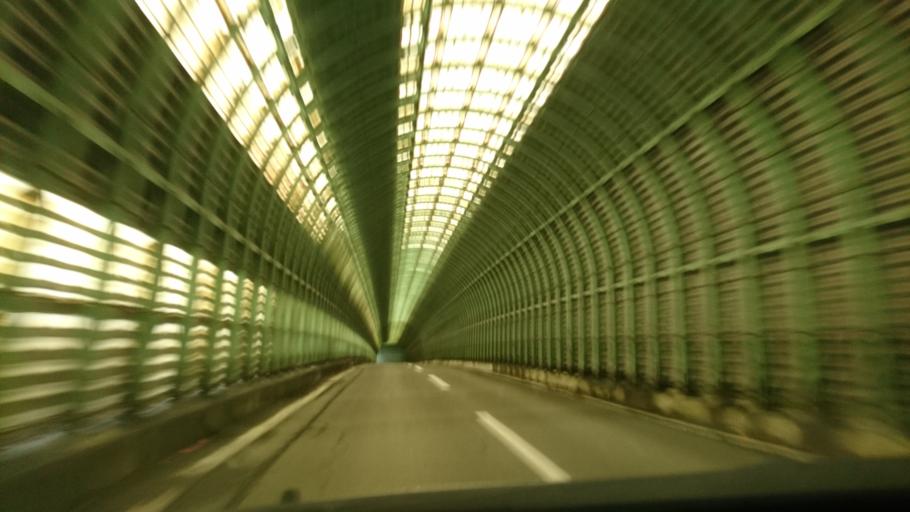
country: JP
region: Iwate
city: Ichinoseki
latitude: 38.9398
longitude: 140.8196
